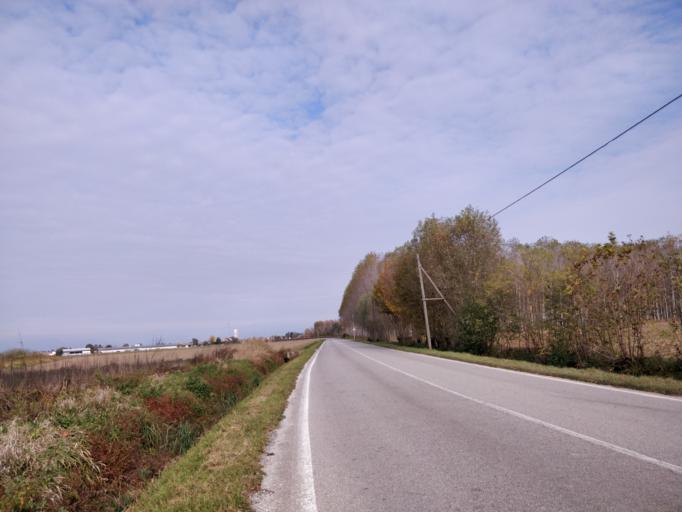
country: IT
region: Friuli Venezia Giulia
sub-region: Provincia di Udine
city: Bertiolo
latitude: 45.9290
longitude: 13.0487
